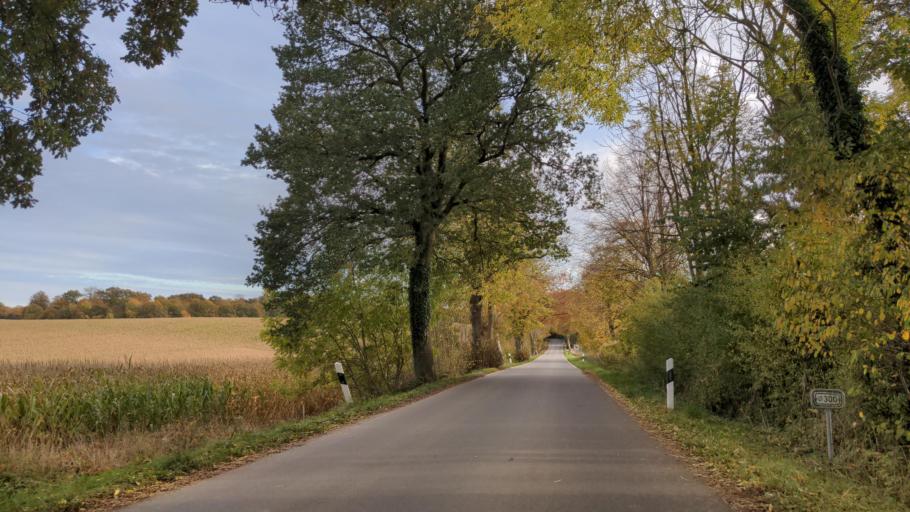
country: DE
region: Schleswig-Holstein
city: Glasau
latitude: 54.1049
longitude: 10.5380
